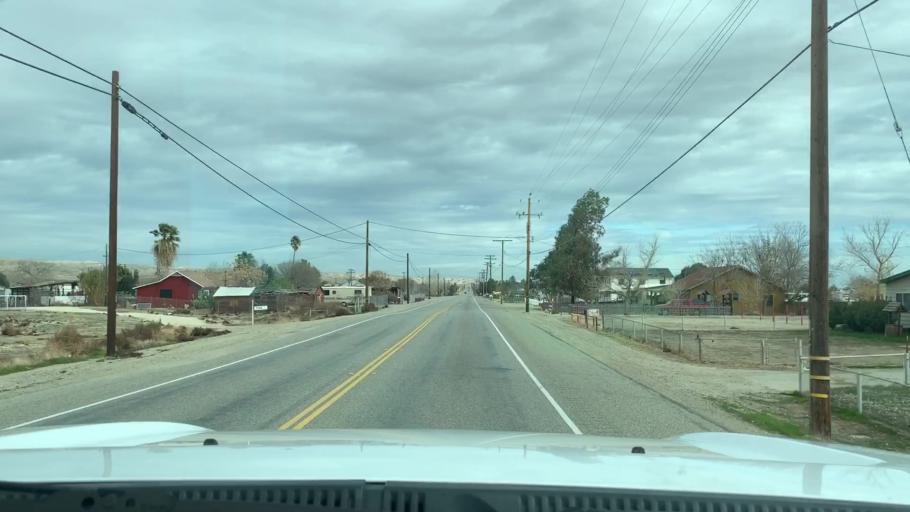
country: US
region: California
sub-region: Kern County
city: Ford City
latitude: 35.2179
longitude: -119.3928
